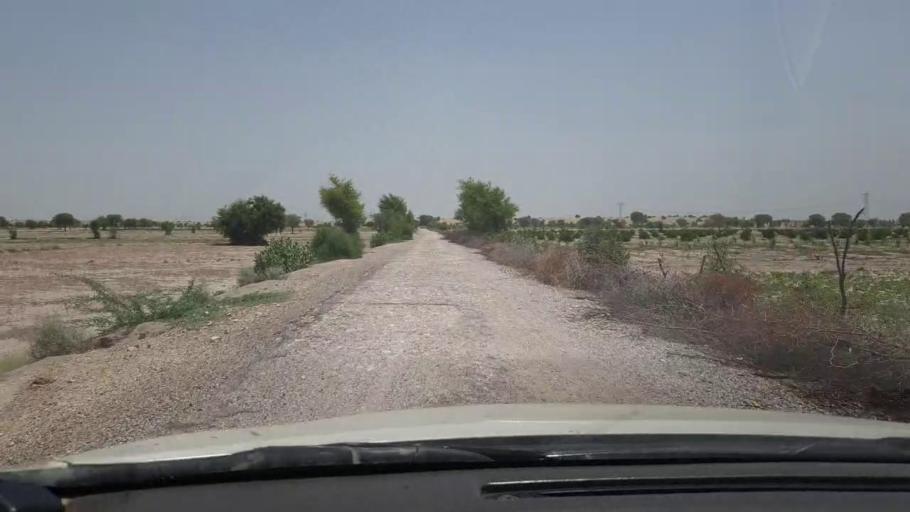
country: PK
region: Sindh
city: Rohri
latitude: 27.5063
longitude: 69.1749
